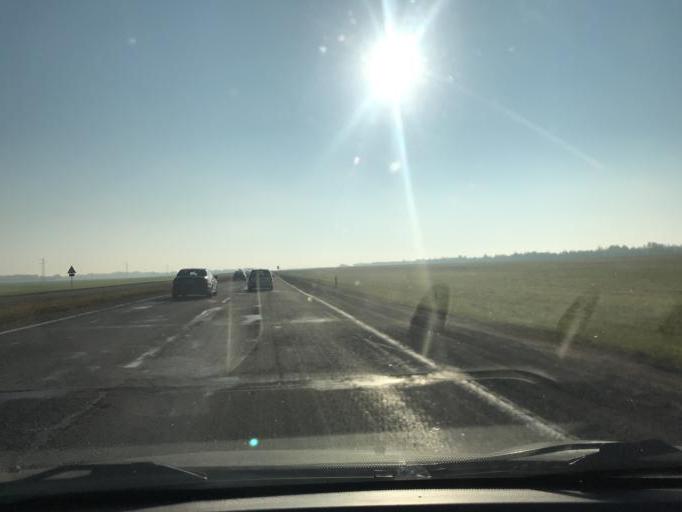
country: BY
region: Minsk
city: Dukora
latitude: 53.6551
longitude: 27.9606
